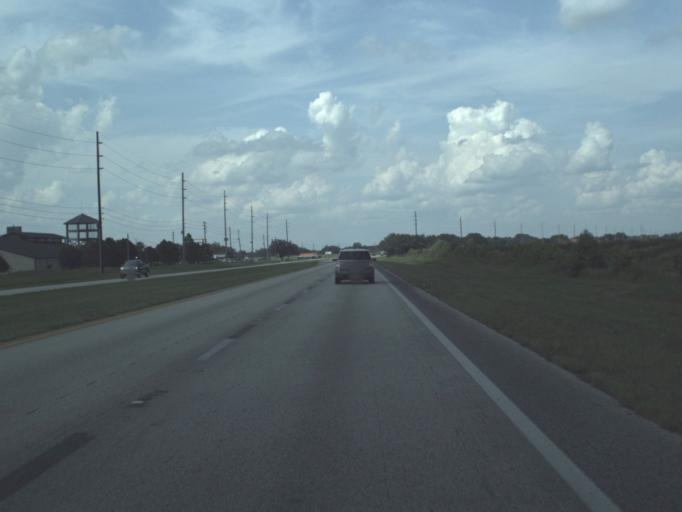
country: US
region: Florida
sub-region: Polk County
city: Lake Wales
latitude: 27.8766
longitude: -81.5960
